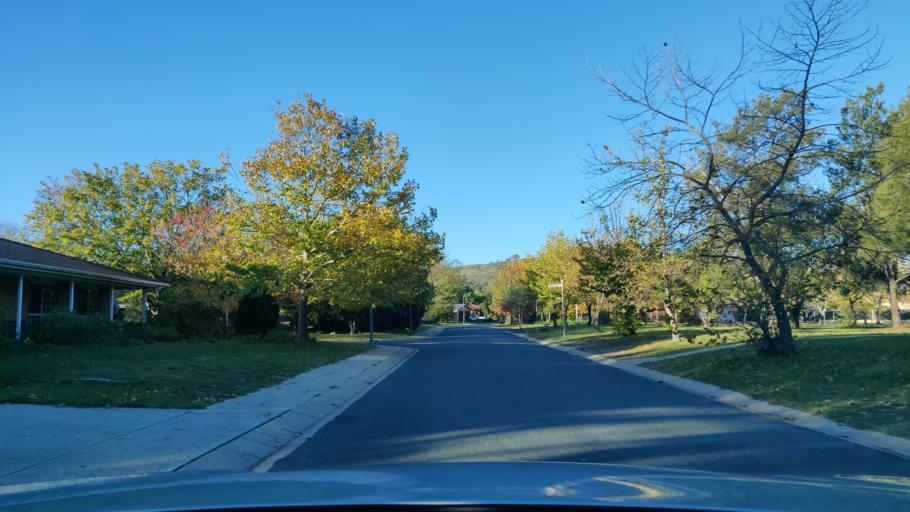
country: AU
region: Australian Capital Territory
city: Macarthur
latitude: -35.4421
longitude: 149.1228
